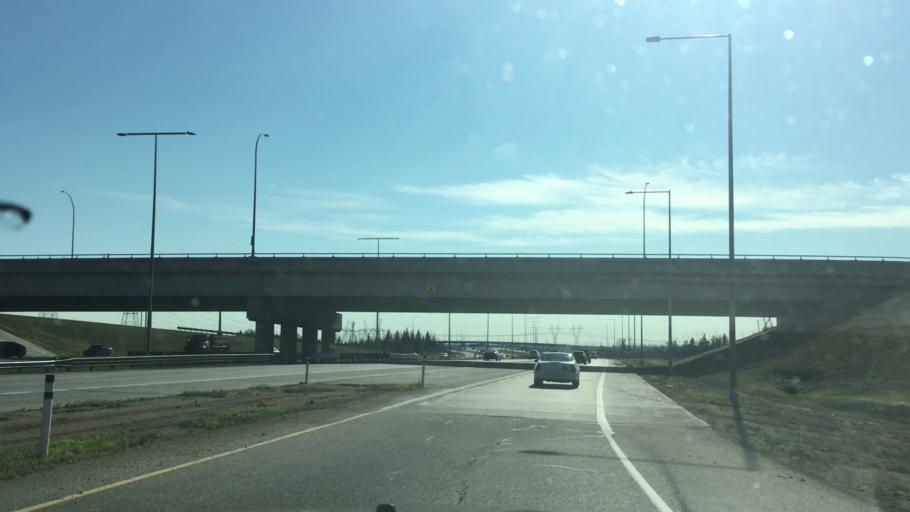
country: CA
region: Alberta
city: Edmonton
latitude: 53.4344
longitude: -113.5209
